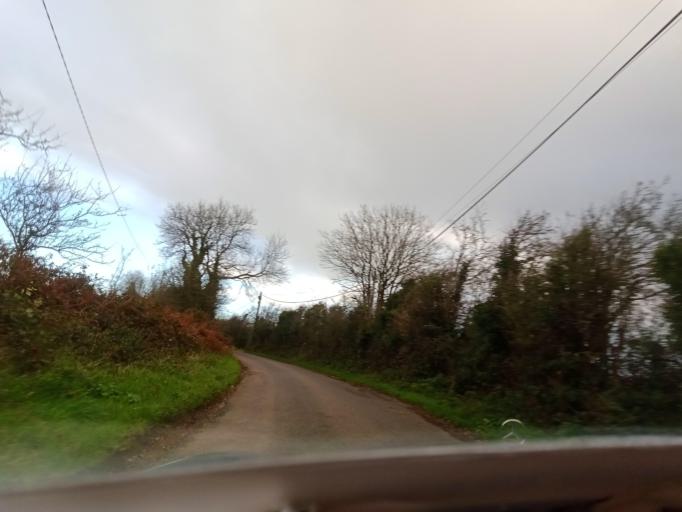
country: IE
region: Munster
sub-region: Waterford
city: Waterford
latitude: 52.3152
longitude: -7.0467
